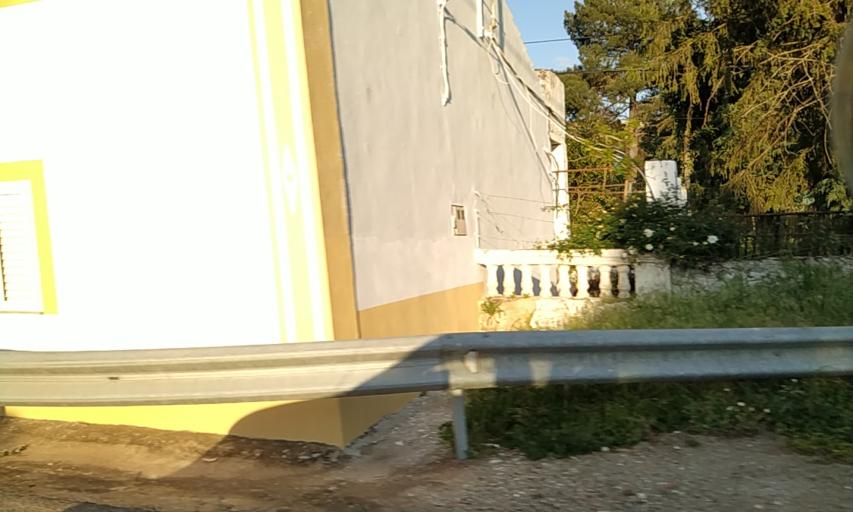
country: ES
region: Extremadura
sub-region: Provincia de Caceres
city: Valencia de Alcantara
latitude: 39.3638
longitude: -7.2724
